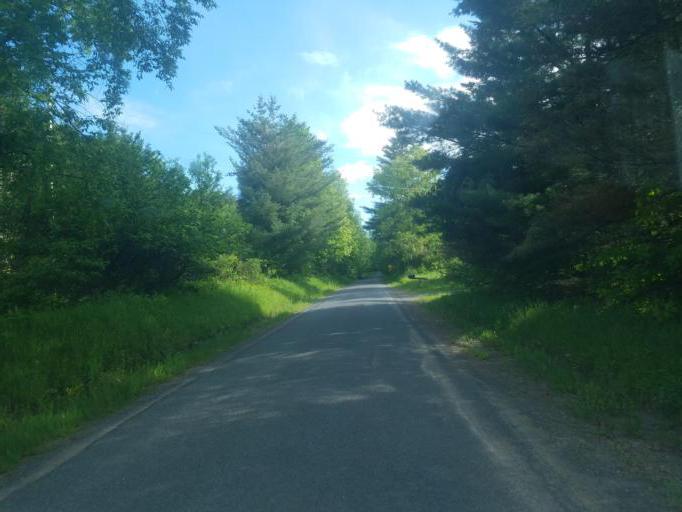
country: US
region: New York
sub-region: Herkimer County
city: Dolgeville
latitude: 43.3231
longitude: -74.9434
